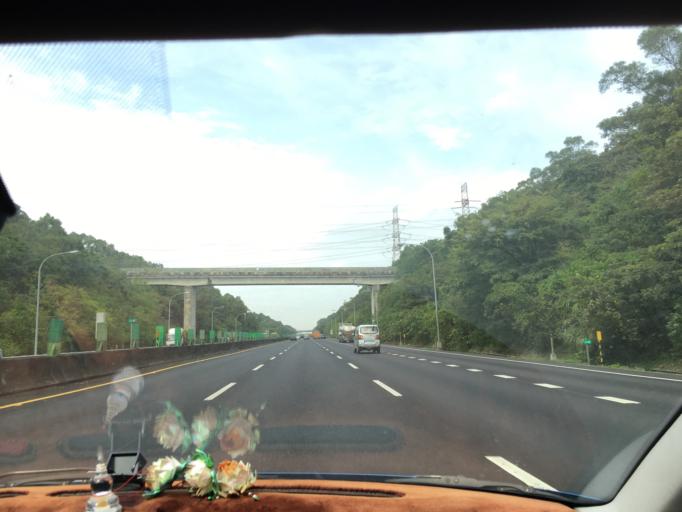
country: TW
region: Taiwan
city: Daxi
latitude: 24.8165
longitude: 121.2005
